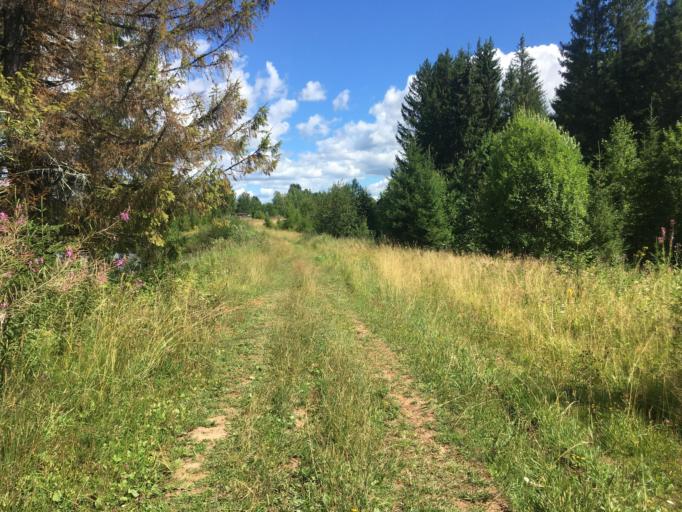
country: RU
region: Perm
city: Komarikhinskiy
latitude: 58.0878
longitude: 57.1036
